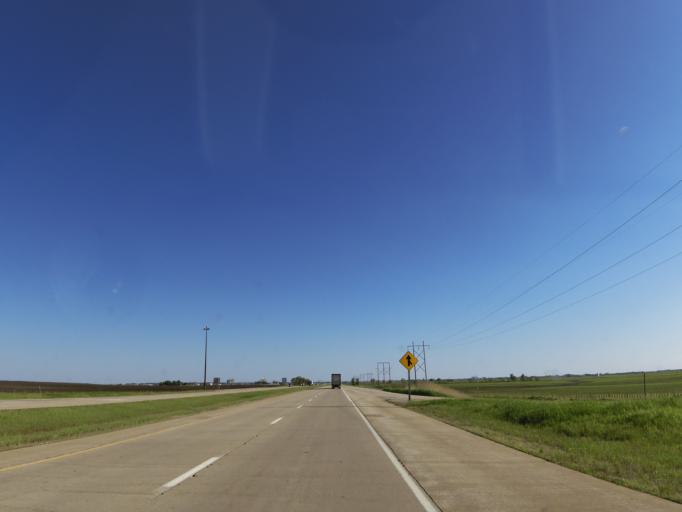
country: US
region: Illinois
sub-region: Marshall County
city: Wenona
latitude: 41.1173
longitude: -89.0755
